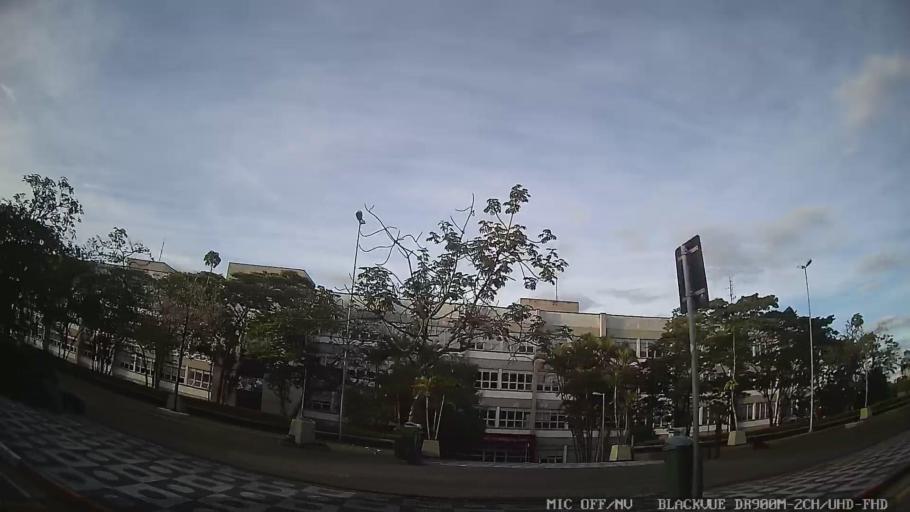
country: BR
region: Sao Paulo
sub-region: Mogi das Cruzes
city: Mogi das Cruzes
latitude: -23.5196
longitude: -46.1851
